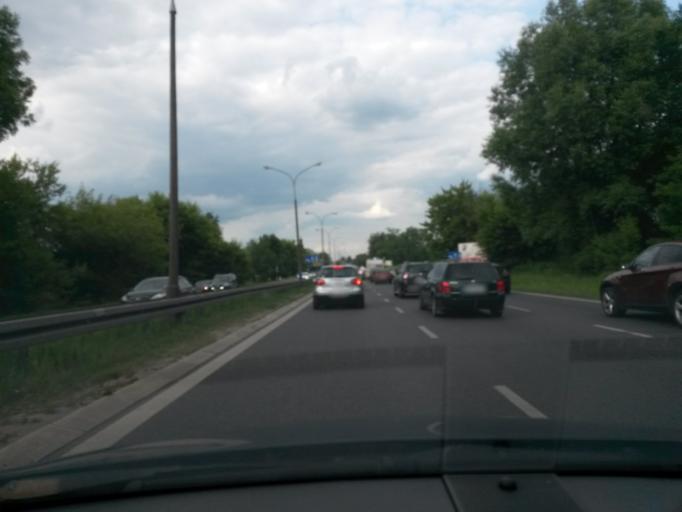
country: PL
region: Masovian Voivodeship
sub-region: Powiat pruszkowski
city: Nowe Grocholice
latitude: 52.1469
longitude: 20.9120
